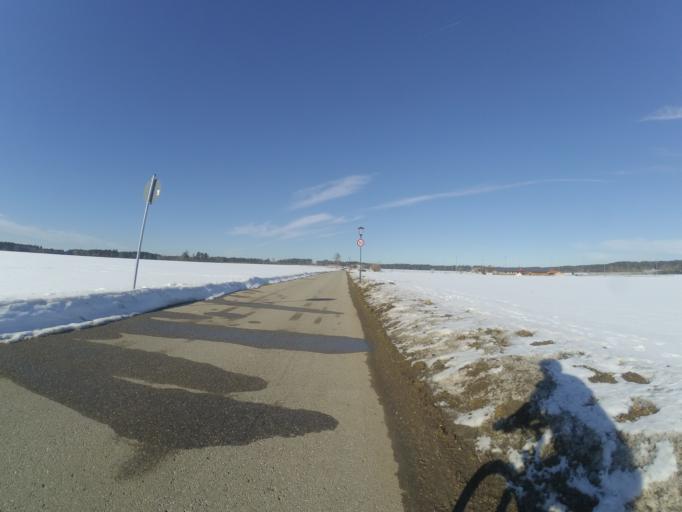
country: DE
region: Bavaria
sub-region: Upper Bavaria
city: Aying
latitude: 47.9736
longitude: 11.7674
